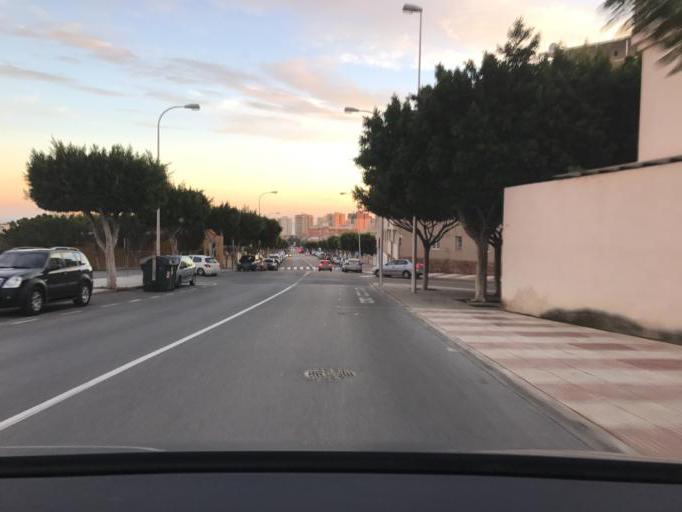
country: ES
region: Andalusia
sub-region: Provincia de Almeria
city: Aguadulce
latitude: 36.8183
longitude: -2.5815
